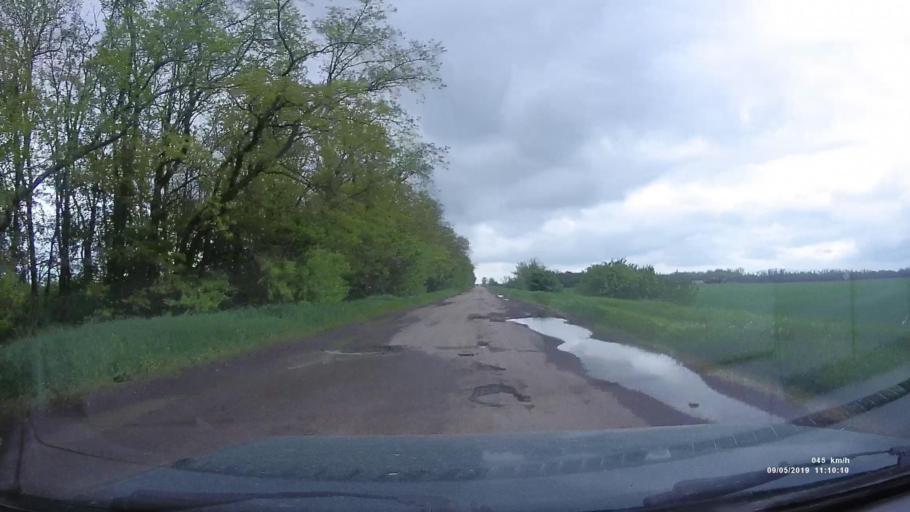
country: RU
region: Krasnodarskiy
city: Kanelovskaya
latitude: 46.7775
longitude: 39.2115
